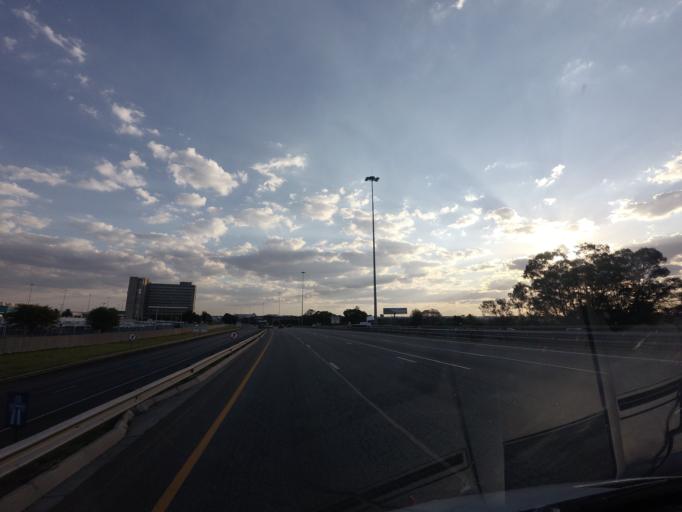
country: ZA
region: Gauteng
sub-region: City of Johannesburg Metropolitan Municipality
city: Modderfontein
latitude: -26.1114
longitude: 28.2386
